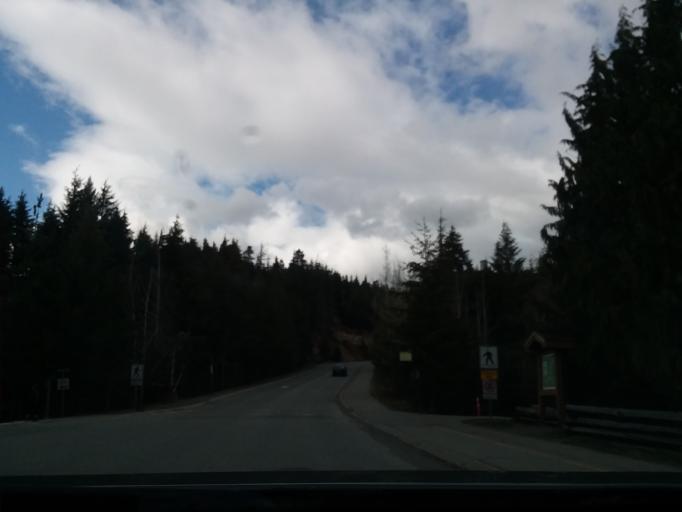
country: CA
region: British Columbia
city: Whistler
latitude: 50.1102
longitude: -122.9711
